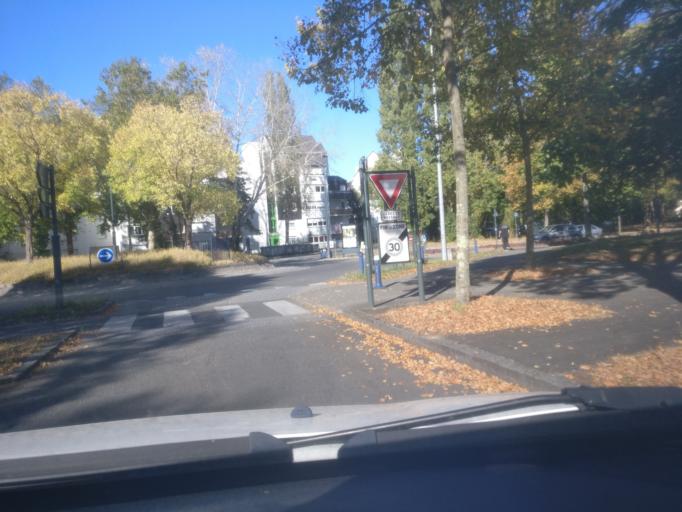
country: FR
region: Brittany
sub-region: Departement d'Ille-et-Vilaine
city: Saint-Gregoire
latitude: 48.1363
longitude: -1.6670
